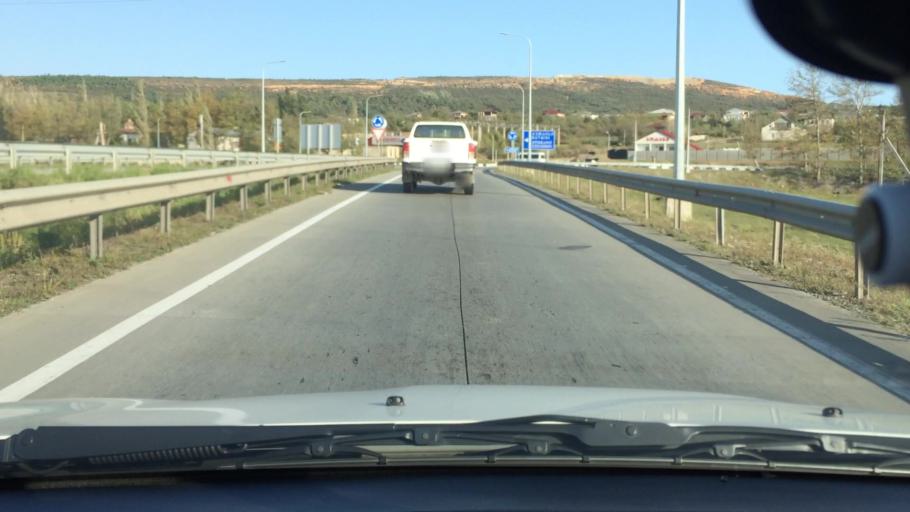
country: GE
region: Imereti
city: Kutaisi
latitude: 42.2123
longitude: 42.8195
